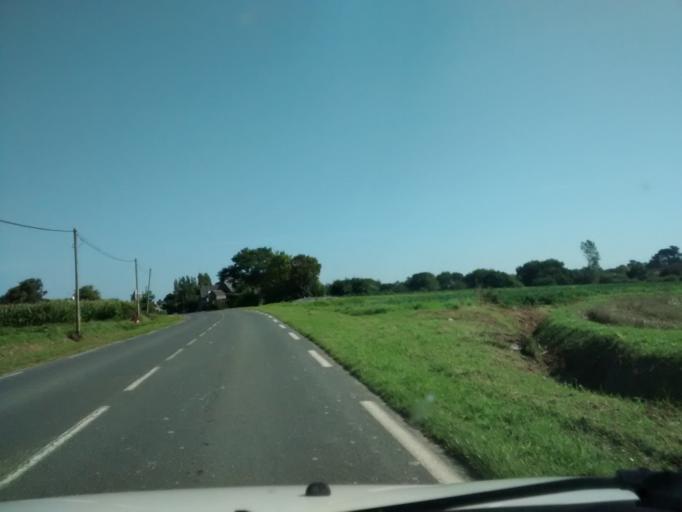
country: FR
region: Brittany
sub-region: Departement des Cotes-d'Armor
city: Pleumeur-Gautier
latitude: 48.8252
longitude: -3.1862
